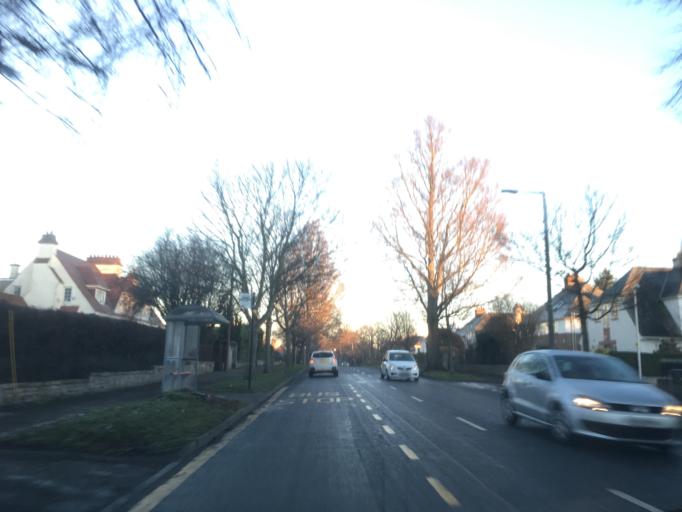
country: GB
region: Scotland
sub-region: Edinburgh
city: Colinton
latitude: 55.9506
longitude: -3.2472
